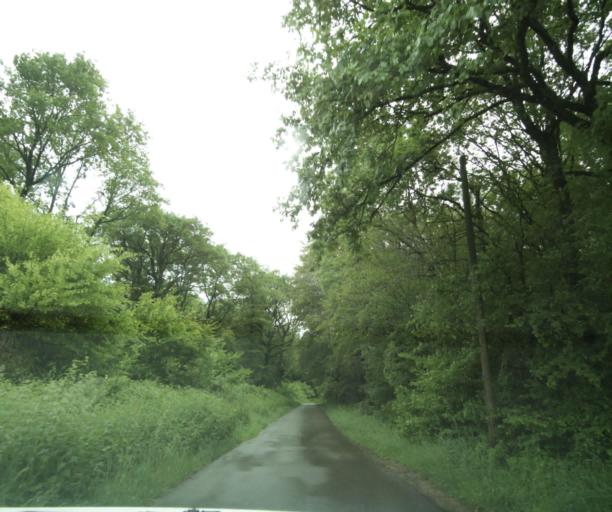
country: FR
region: Bourgogne
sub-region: Departement de Saone-et-Loire
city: Ciry-le-Noble
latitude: 46.5201
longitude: 4.3019
